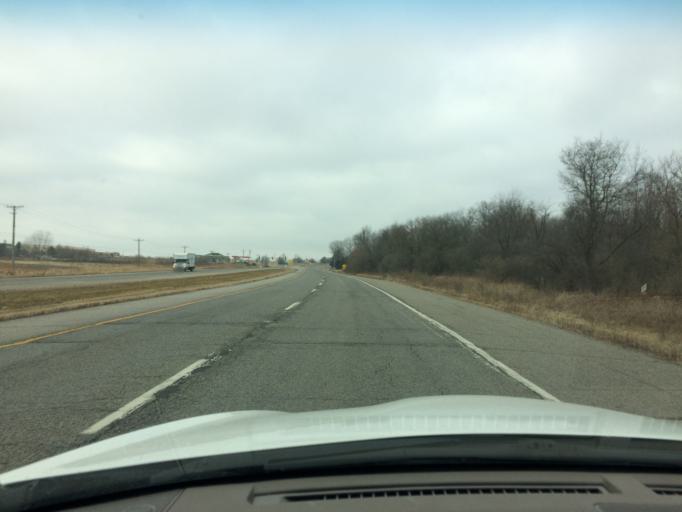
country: US
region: Illinois
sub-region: Kane County
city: Sugar Grove
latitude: 41.7877
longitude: -88.4530
